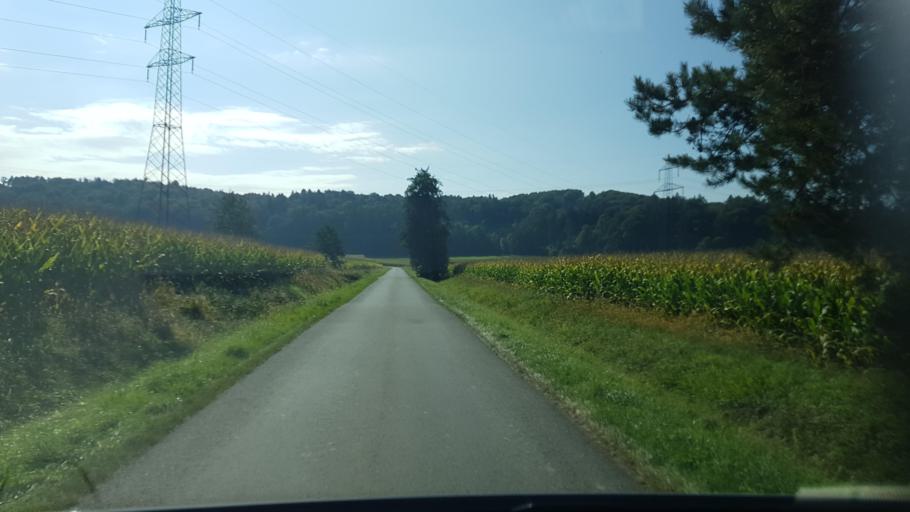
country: AT
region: Styria
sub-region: Politischer Bezirk Deutschlandsberg
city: Wettmannstatten
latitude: 46.8266
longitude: 15.3551
